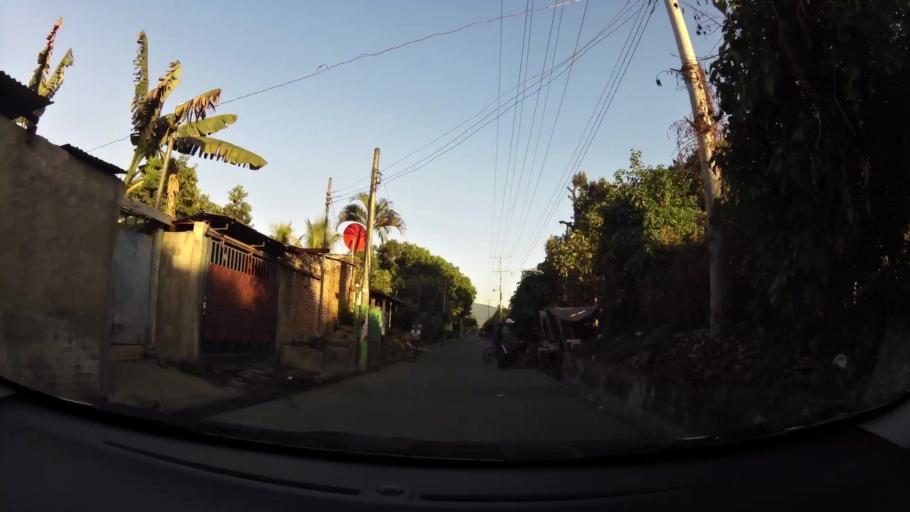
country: SV
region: Sonsonate
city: Armenia
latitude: 13.7422
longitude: -89.4005
